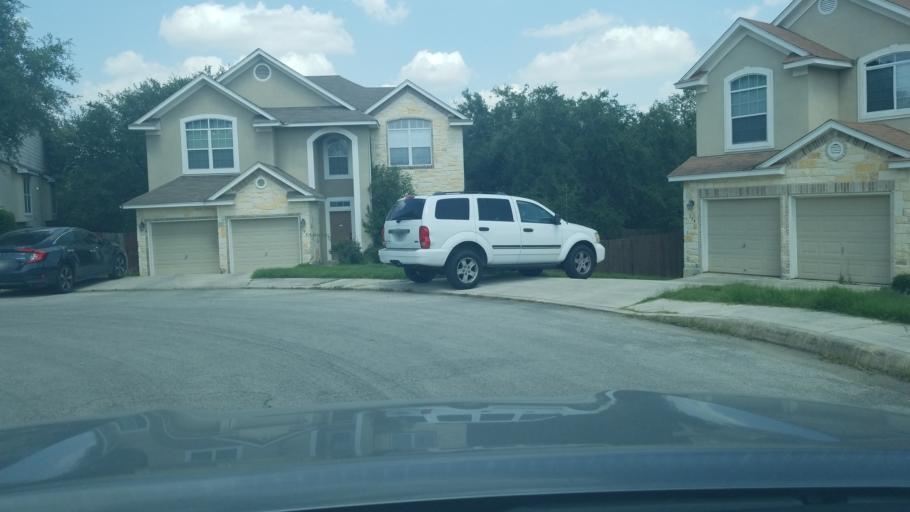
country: US
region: Texas
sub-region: Bexar County
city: Timberwood Park
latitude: 29.6602
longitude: -98.4953
